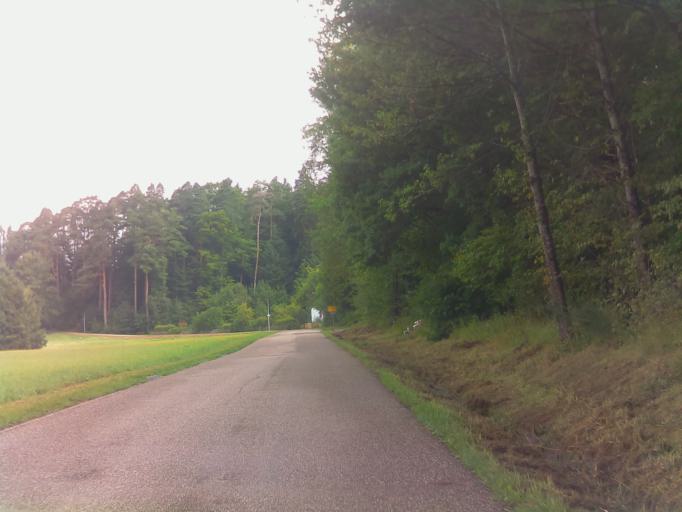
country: DE
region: Baden-Wuerttemberg
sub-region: Karlsruhe Region
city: Dobel
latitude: 48.7927
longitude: 8.5043
